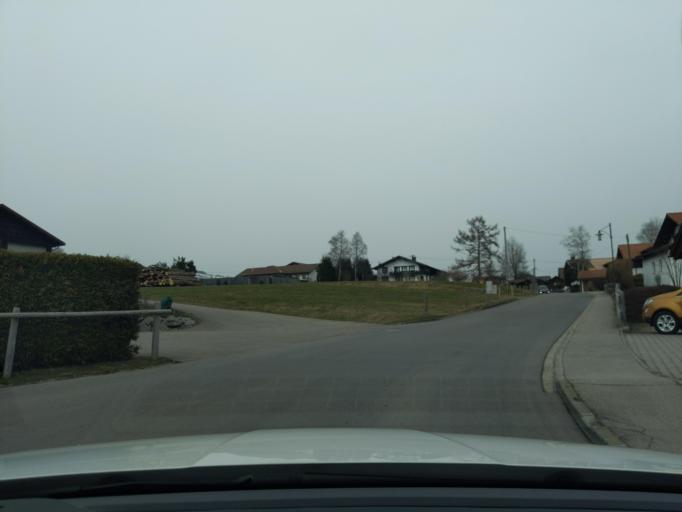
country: DE
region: Bavaria
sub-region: Swabia
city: Ofterschwang
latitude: 47.4865
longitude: 10.2633
